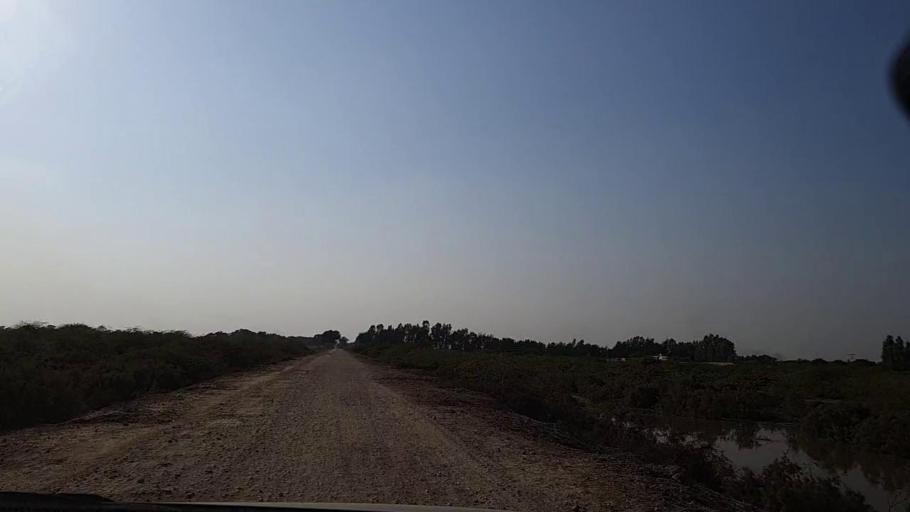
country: PK
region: Sindh
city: Mirwah Gorchani
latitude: 25.2240
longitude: 68.9621
